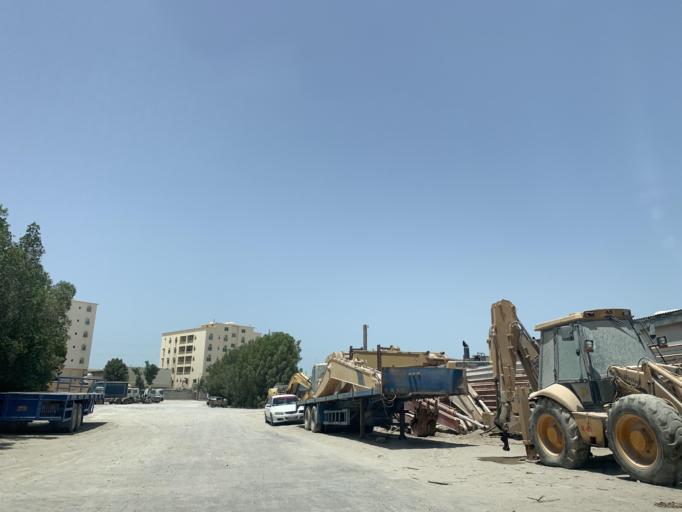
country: BH
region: Northern
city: Sitrah
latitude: 26.1744
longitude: 50.6064
